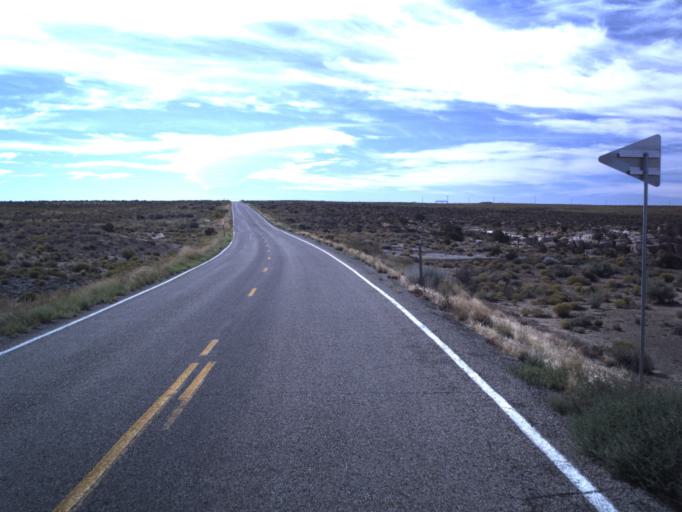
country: US
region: Utah
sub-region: San Juan County
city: Blanding
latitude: 37.3380
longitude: -109.3490
